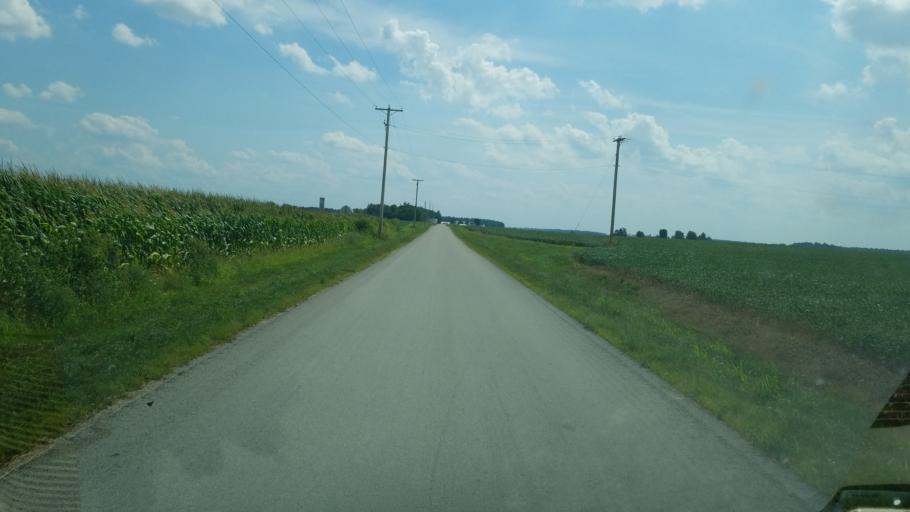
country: US
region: Ohio
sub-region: Hardin County
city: Forest
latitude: 40.7862
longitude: -83.4679
